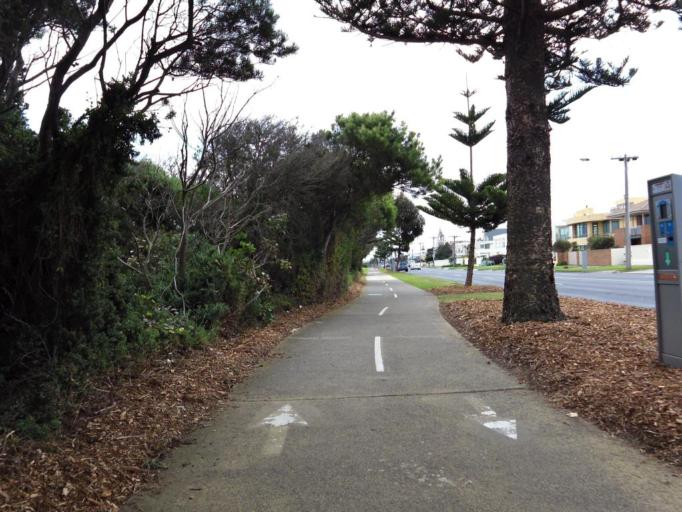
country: AU
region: Victoria
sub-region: Bayside
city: Hampton
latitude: -37.9374
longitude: 144.9979
